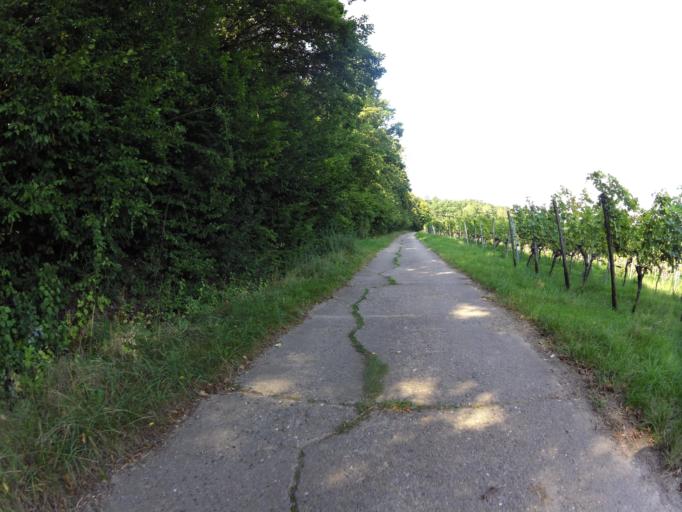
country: DE
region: Bavaria
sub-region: Regierungsbezirk Unterfranken
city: Nordheim
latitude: 49.8455
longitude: 10.1649
